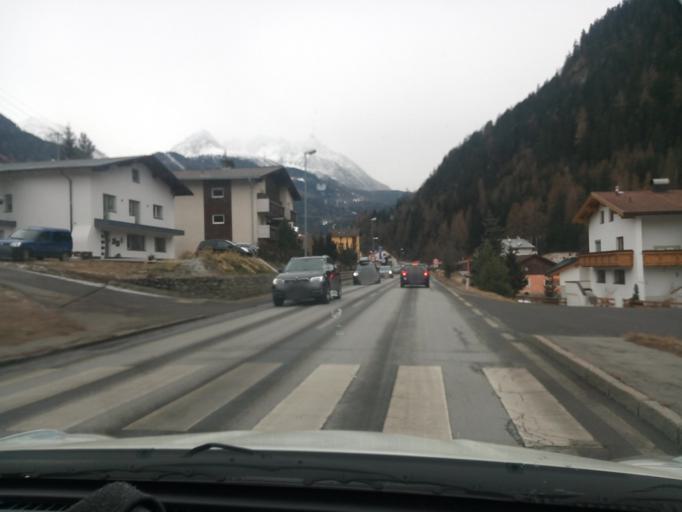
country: AT
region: Tyrol
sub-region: Politischer Bezirk Landeck
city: Nauders
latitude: 46.8892
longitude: 10.5000
